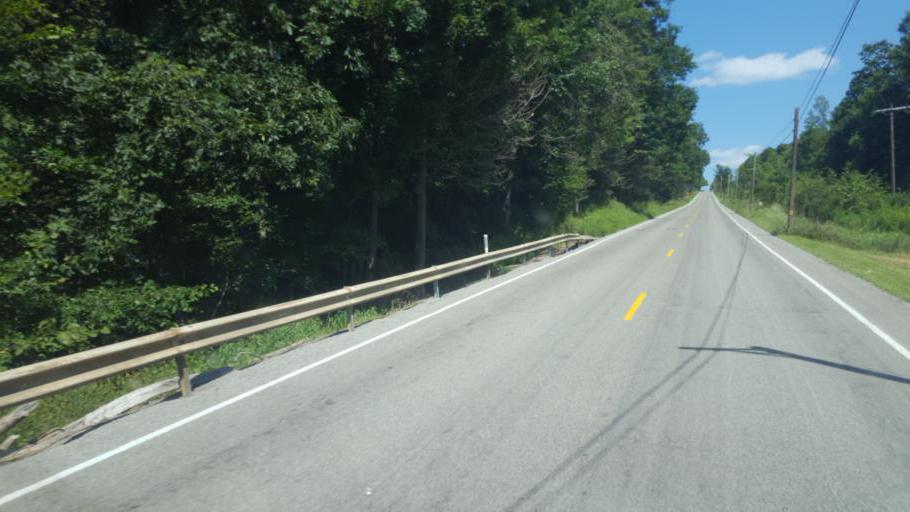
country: US
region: Pennsylvania
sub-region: Clarion County
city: Knox
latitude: 41.1048
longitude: -79.6414
